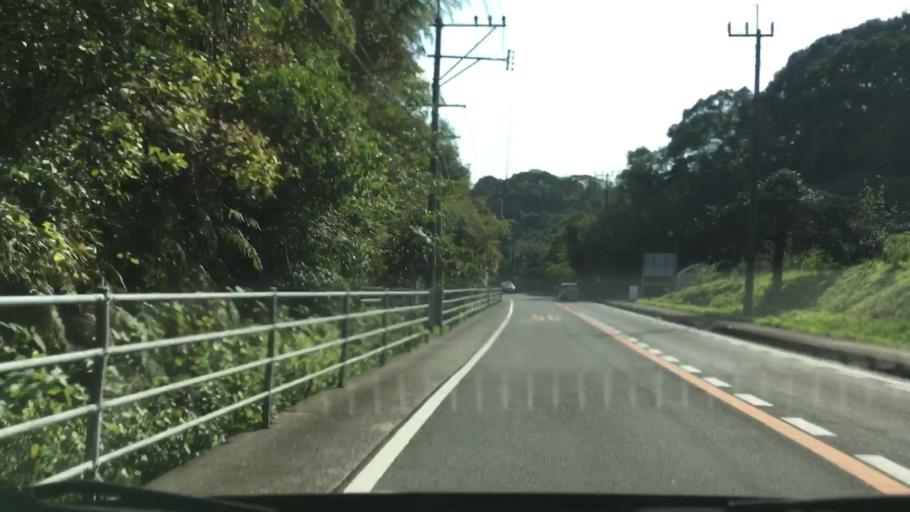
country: JP
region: Nagasaki
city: Togitsu
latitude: 32.9585
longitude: 129.7824
